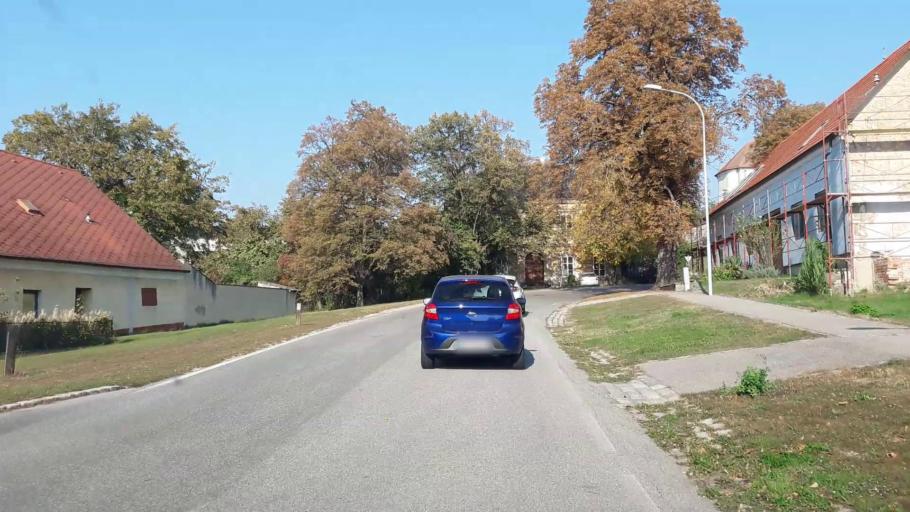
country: AT
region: Lower Austria
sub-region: Politischer Bezirk Ganserndorf
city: Marchegg
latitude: 48.2217
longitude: 16.9028
